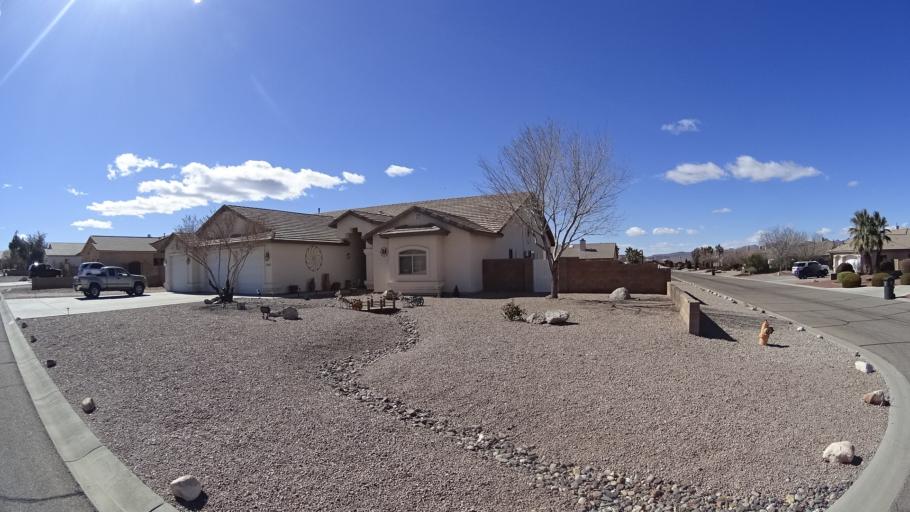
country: US
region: Arizona
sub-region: Mohave County
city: New Kingman-Butler
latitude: 35.2097
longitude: -113.9727
